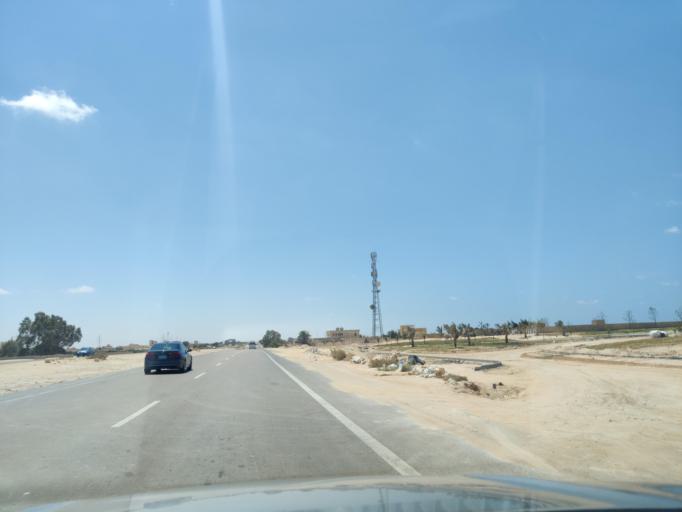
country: EG
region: Muhafazat Matruh
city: Al `Alamayn
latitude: 31.0698
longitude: 28.1382
